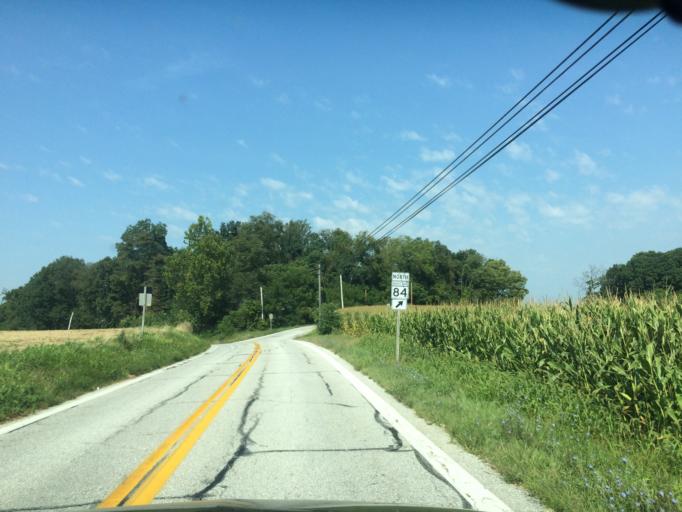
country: US
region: Maryland
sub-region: Carroll County
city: New Windsor
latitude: 39.5575
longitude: -77.1181
